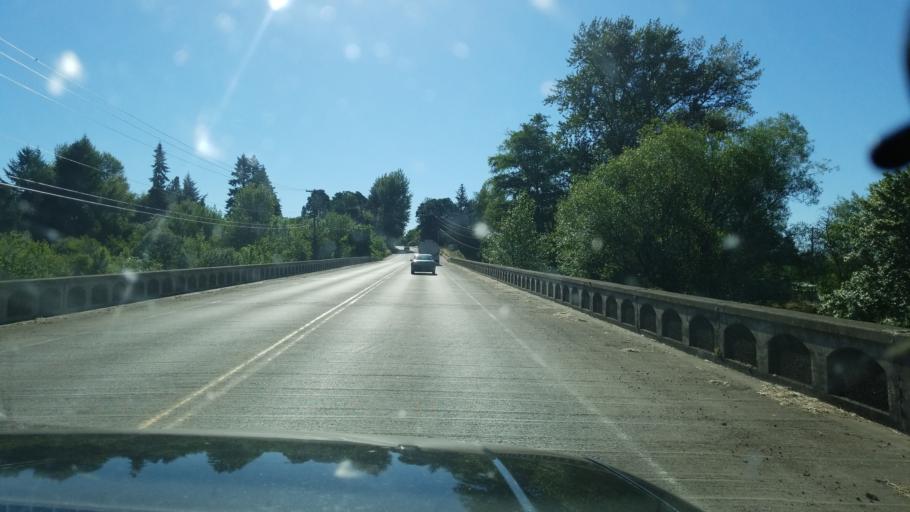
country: US
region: Oregon
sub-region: Yamhill County
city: Carlton
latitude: 45.2941
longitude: -123.1877
